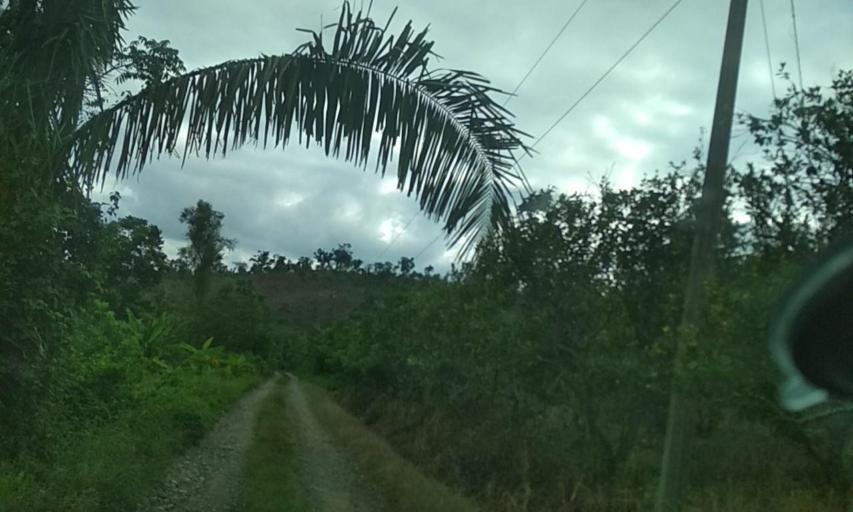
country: MX
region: Veracruz
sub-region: Papantla
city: Polutla
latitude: 20.5886
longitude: -97.2783
